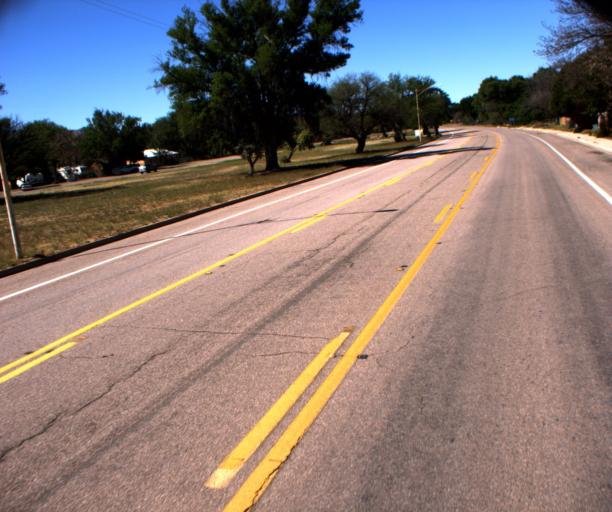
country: US
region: Arizona
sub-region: Santa Cruz County
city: Rio Rico
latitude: 31.5389
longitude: -110.7570
